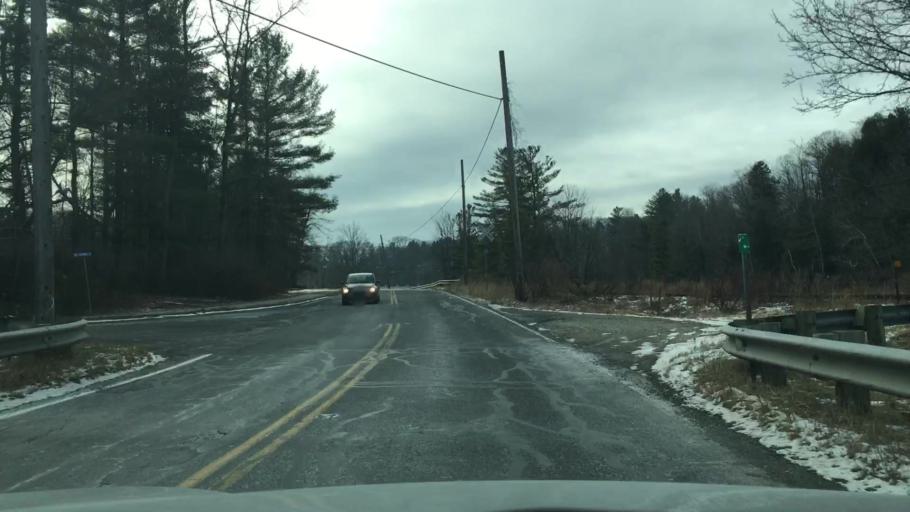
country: US
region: Massachusetts
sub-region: Berkshire County
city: Lee
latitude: 42.3199
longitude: -73.2423
